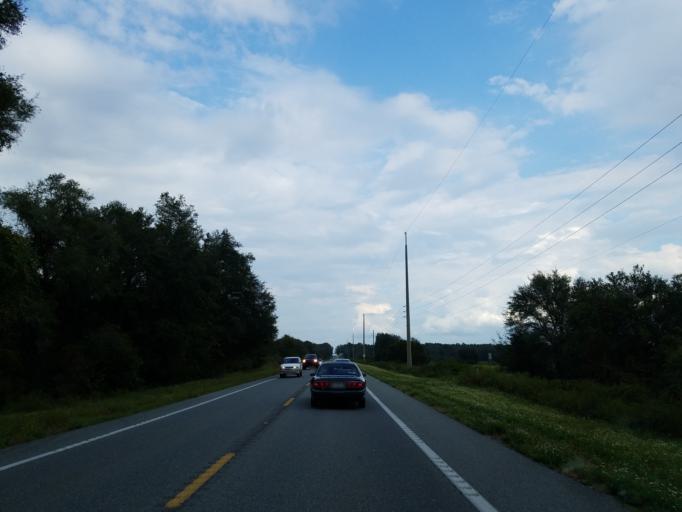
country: US
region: Florida
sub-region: Citrus County
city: Hernando
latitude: 29.0432
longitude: -82.2939
